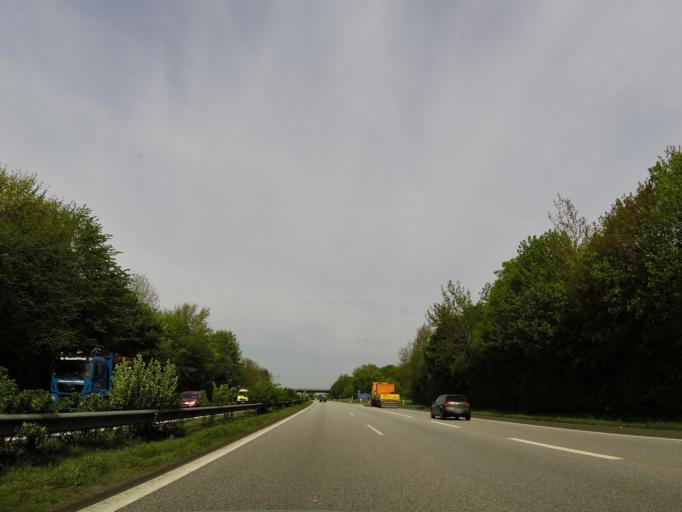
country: DE
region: Schleswig-Holstein
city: Ellerhoop
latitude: 53.7148
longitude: 9.7598
